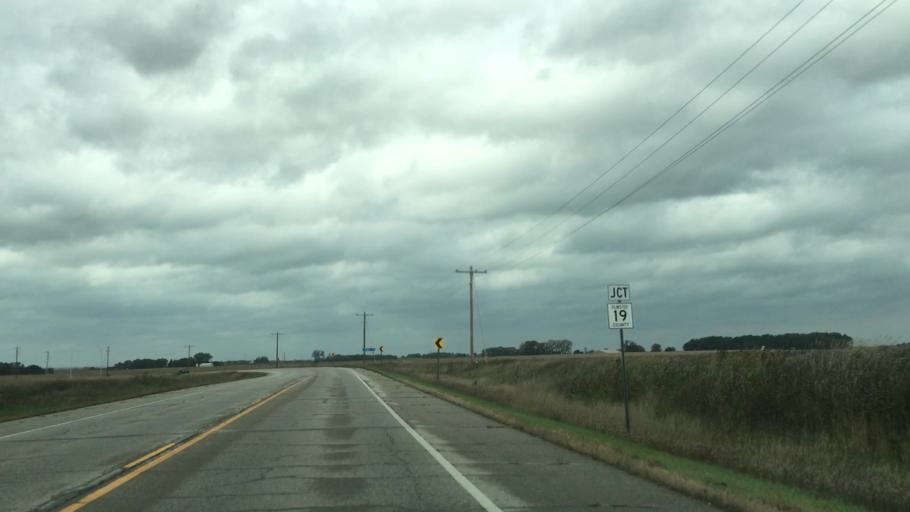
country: US
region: Minnesota
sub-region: Olmsted County
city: Eyota
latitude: 43.9327
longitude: -92.2951
